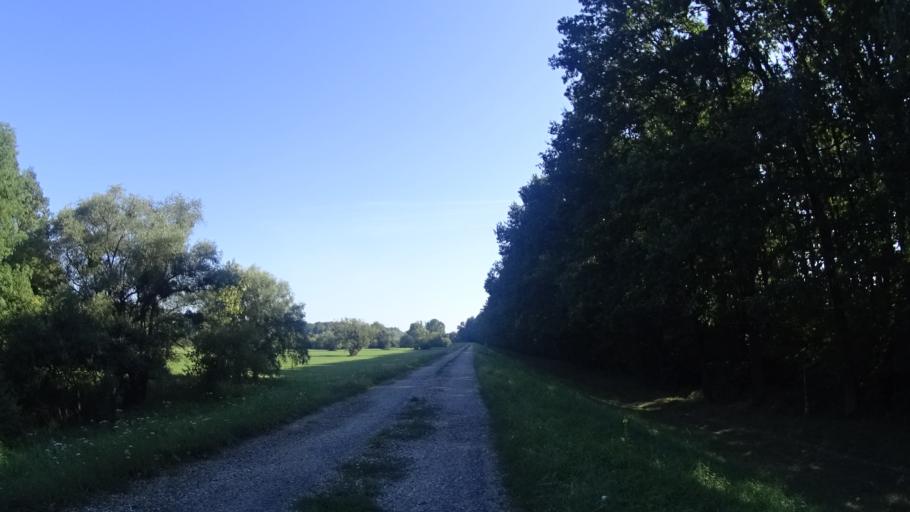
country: CZ
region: South Moravian
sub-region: Okres Breclav
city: Lanzhot
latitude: 48.6637
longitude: 16.9802
